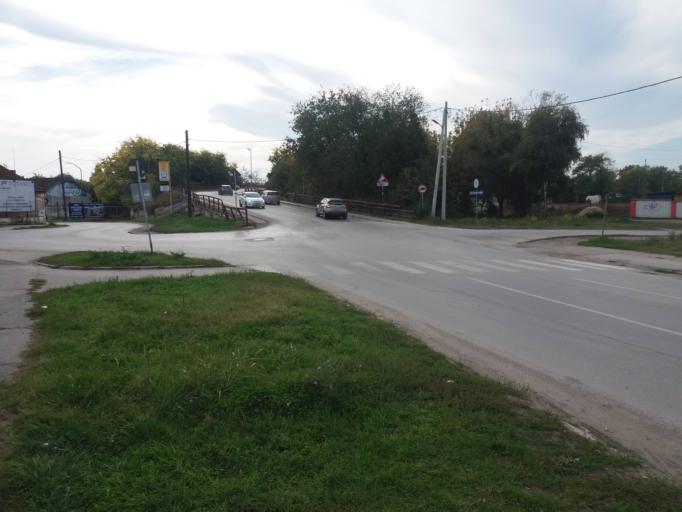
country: RS
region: Autonomna Pokrajina Vojvodina
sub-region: Severnobacki Okrug
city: Subotica
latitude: 46.1098
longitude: 19.6691
